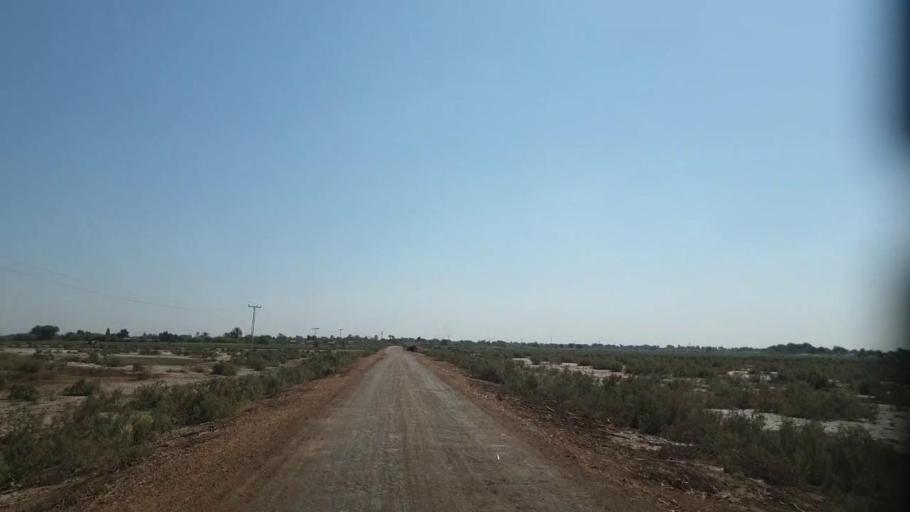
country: PK
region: Sindh
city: Mirpur Khas
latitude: 25.5865
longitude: 69.1087
